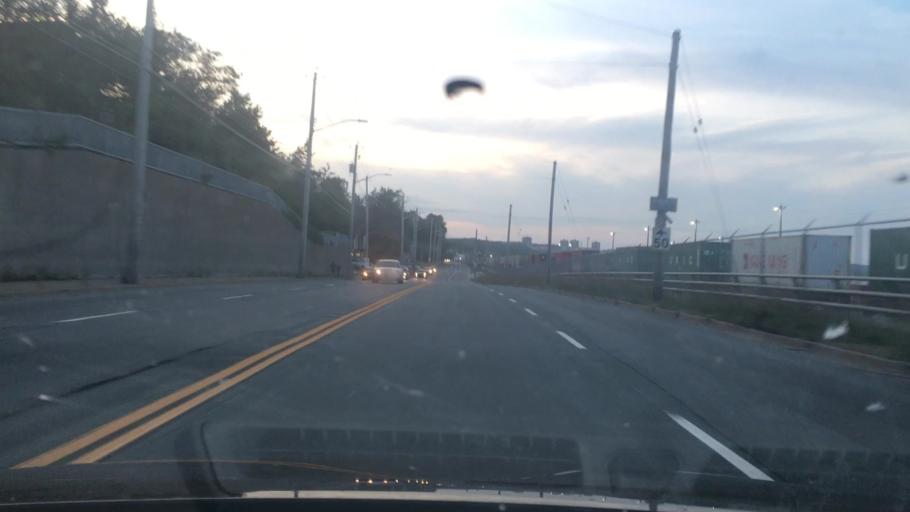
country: CA
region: Nova Scotia
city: Dartmouth
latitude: 44.6689
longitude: -63.6398
